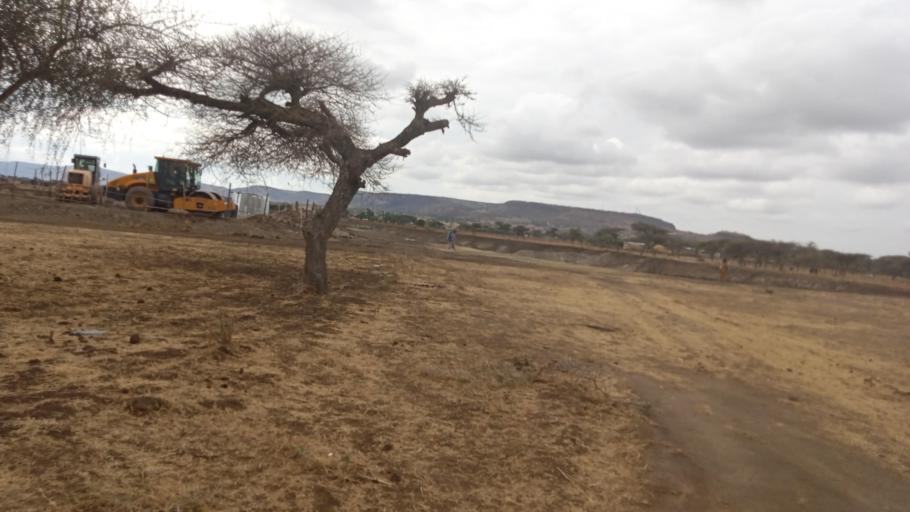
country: ET
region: Oromiya
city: Ziway
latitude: 7.9210
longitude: 38.6829
